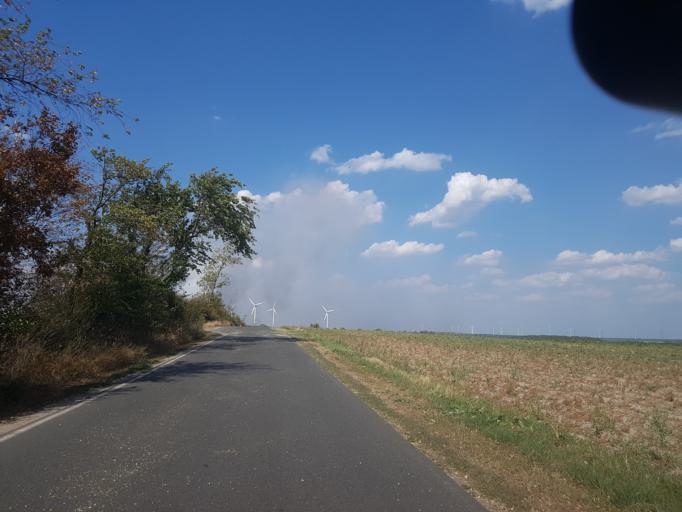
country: DE
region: Brandenburg
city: Niedergorsdorf
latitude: 51.9873
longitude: 12.8949
